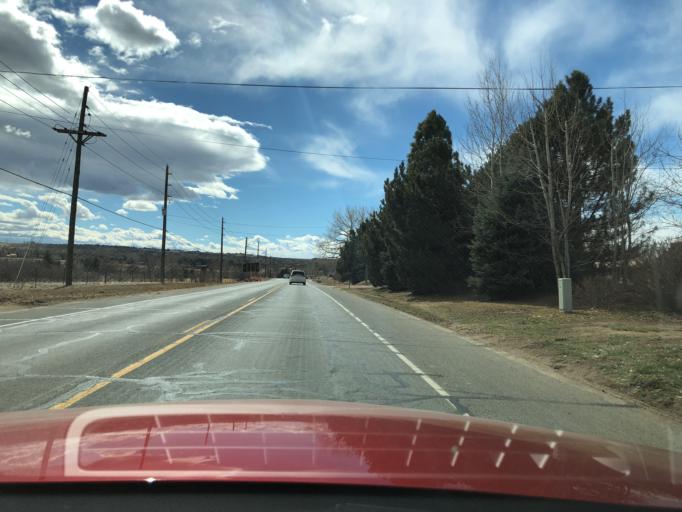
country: US
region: Colorado
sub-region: Boulder County
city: Gunbarrel
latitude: 40.0187
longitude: -105.1784
